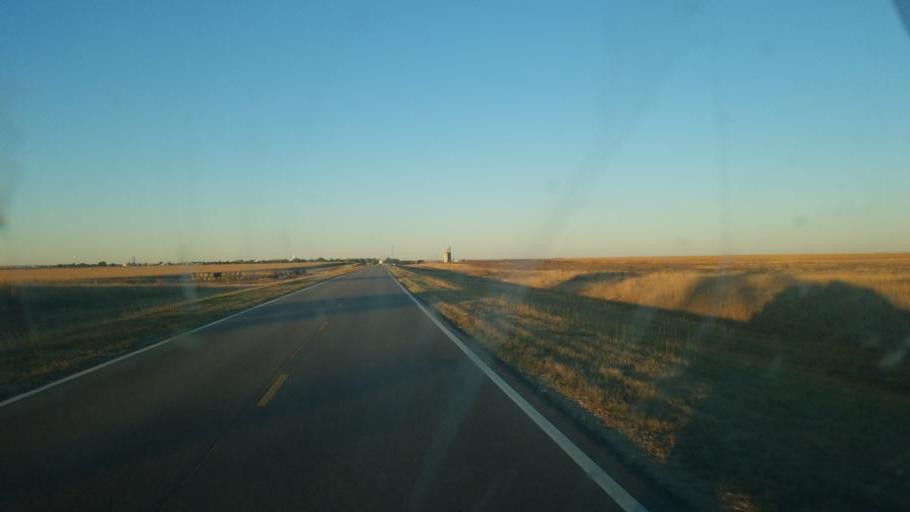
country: US
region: Kansas
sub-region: Wallace County
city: Sharon Springs
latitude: 38.8732
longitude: -101.9429
